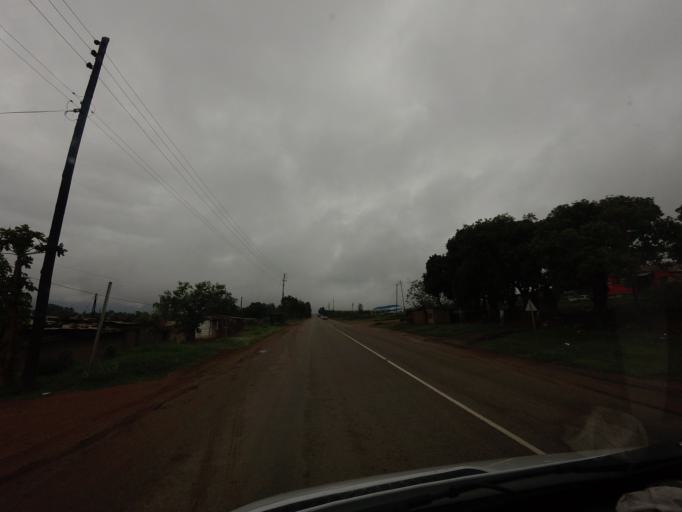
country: SZ
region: Manzini
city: Malkerns
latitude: -26.5326
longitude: 31.1898
